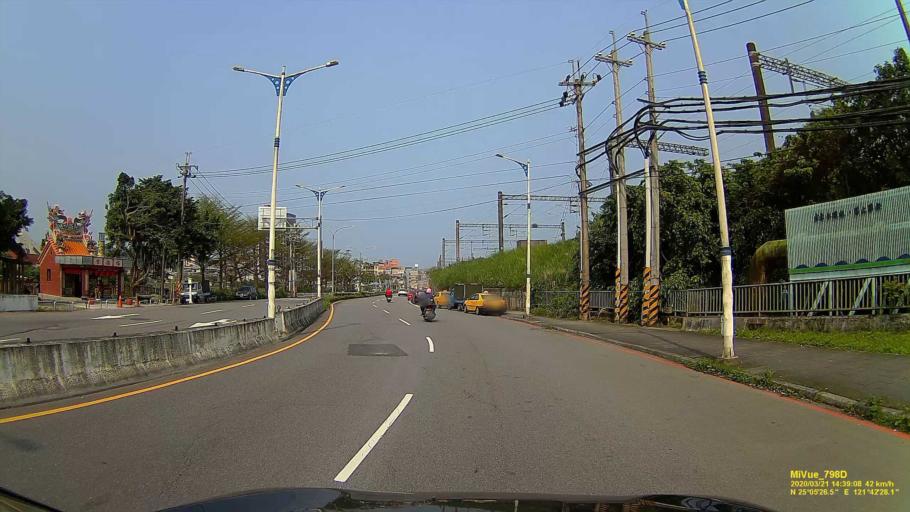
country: TW
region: Taiwan
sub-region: Keelung
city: Keelung
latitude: 25.0899
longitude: 121.7078
